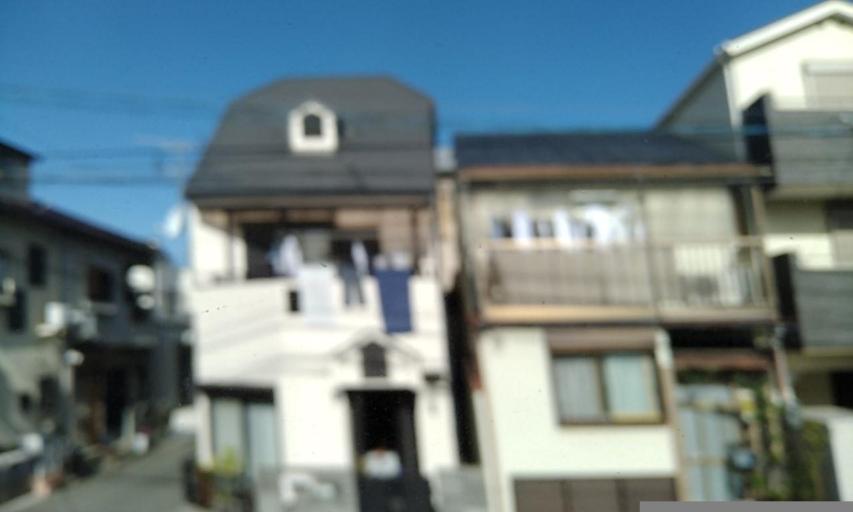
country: JP
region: Hyogo
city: Itami
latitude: 34.7527
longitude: 135.4081
